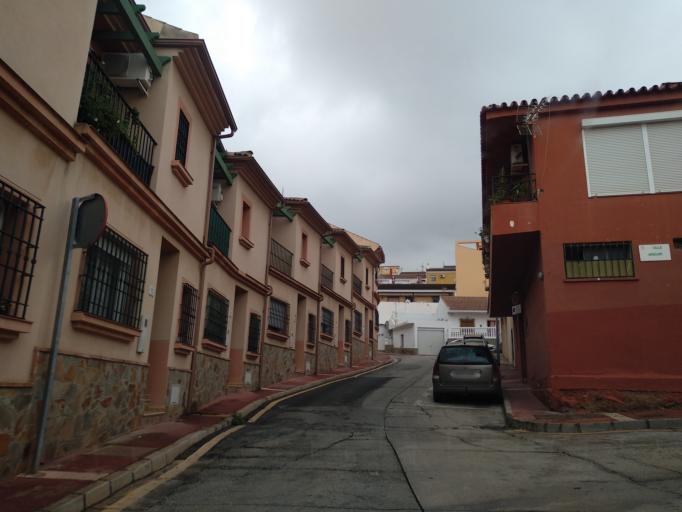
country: ES
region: Andalusia
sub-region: Provincia de Malaga
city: Malaga
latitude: 36.7428
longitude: -4.4786
